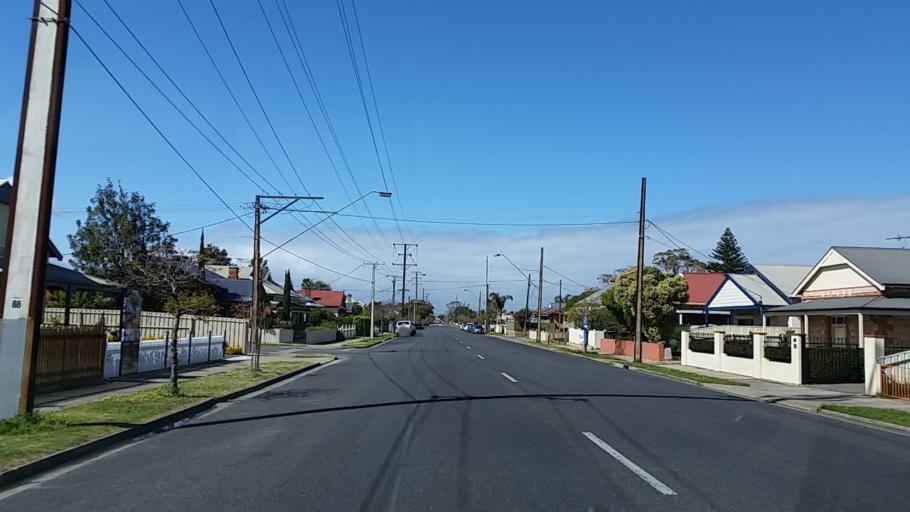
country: AU
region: South Australia
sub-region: Port Adelaide Enfield
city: Birkenhead
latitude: -34.8264
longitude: 138.4954
